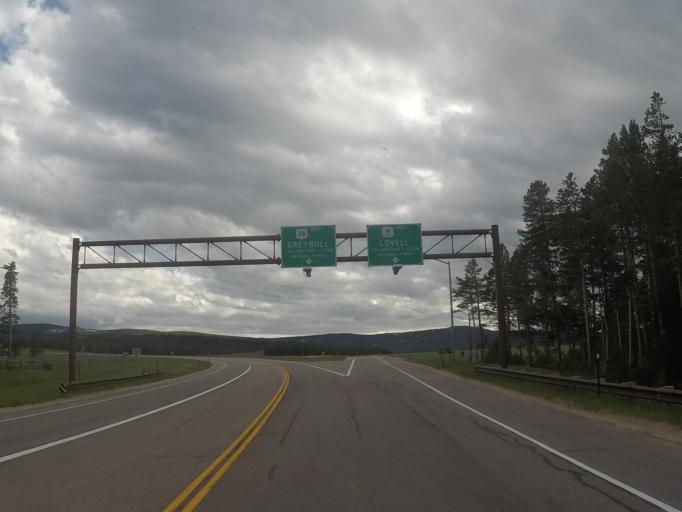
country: US
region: Wyoming
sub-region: Sheridan County
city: Sheridan
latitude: 44.7735
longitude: -107.5158
